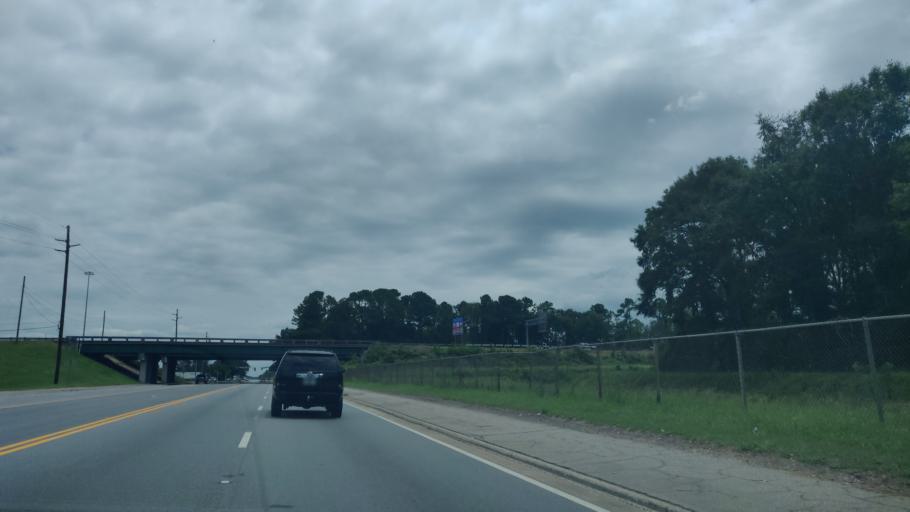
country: US
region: Georgia
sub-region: Dougherty County
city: Albany
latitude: 31.5798
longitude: -84.1134
